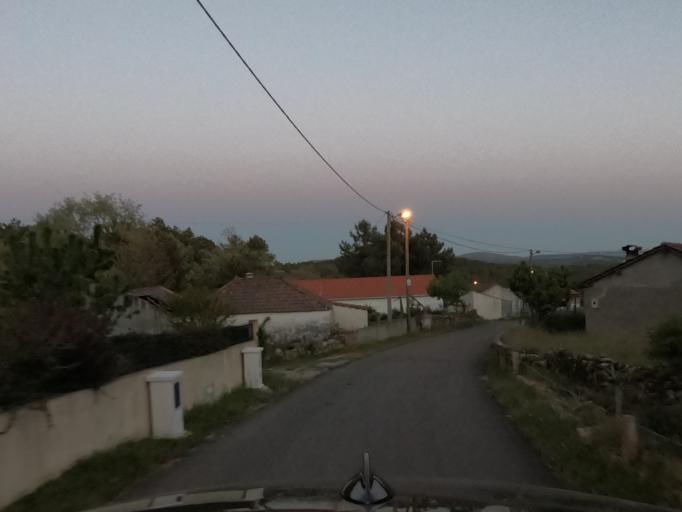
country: PT
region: Vila Real
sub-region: Vila Real
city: Vila Real
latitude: 41.2947
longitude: -7.6817
